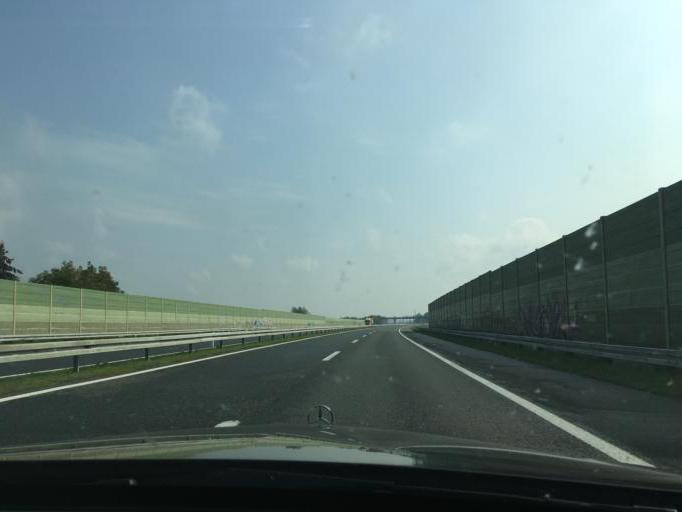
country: HR
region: Brodsko-Posavska
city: Podvinje
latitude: 45.1845
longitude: 18.0251
